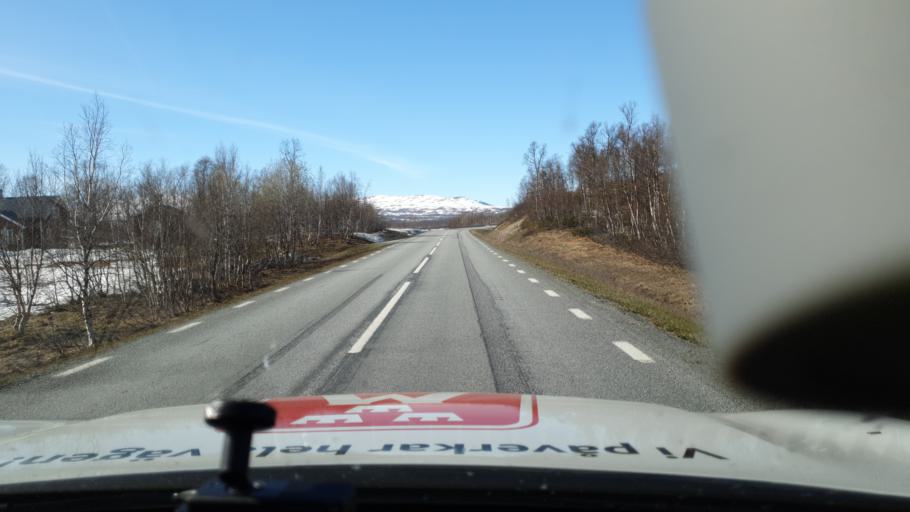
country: NO
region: Nordland
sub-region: Rana
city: Mo i Rana
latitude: 66.0129
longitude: 15.0930
